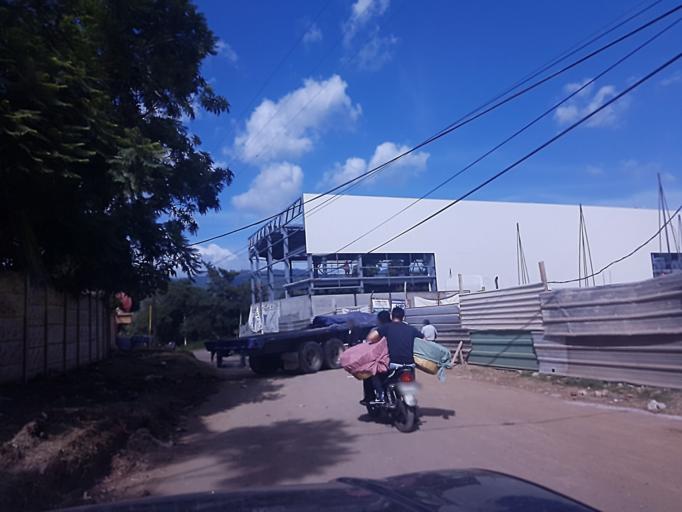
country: GT
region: Guatemala
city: Petapa
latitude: 14.5040
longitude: -90.5576
